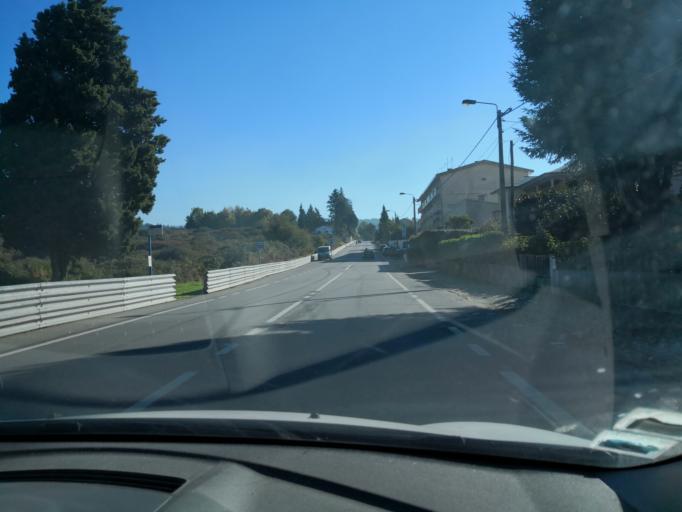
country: PT
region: Vila Real
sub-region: Vila Real
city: Vila Real
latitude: 41.2978
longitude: -7.7235
